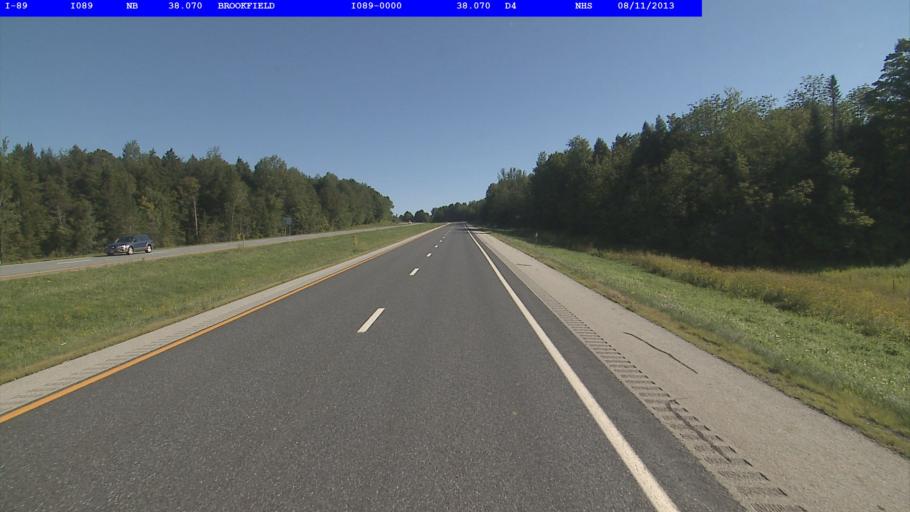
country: US
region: Vermont
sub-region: Orange County
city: Williamstown
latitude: 44.0465
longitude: -72.6073
